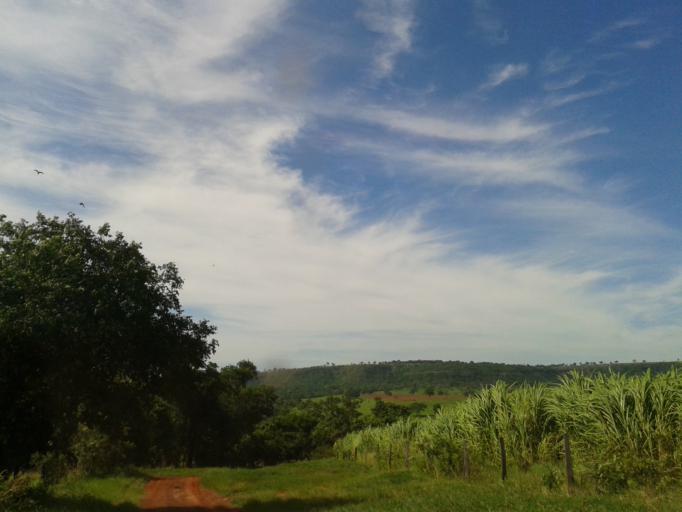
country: BR
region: Minas Gerais
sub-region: Santa Vitoria
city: Santa Vitoria
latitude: -19.0844
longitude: -50.0157
